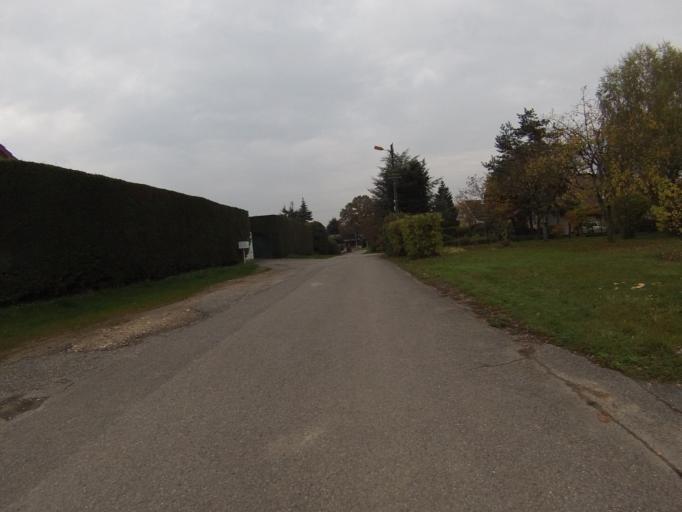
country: FR
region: Rhone-Alpes
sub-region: Departement de l'Ain
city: Ornex
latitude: 46.2561
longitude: 6.0885
